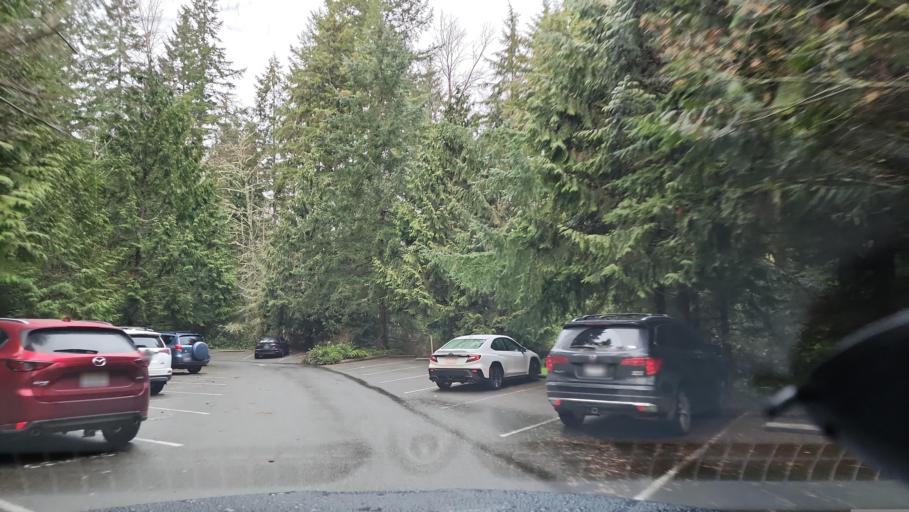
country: US
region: Washington
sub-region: King County
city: Union Hill-Novelty Hill
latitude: 47.6964
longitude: -122.0510
